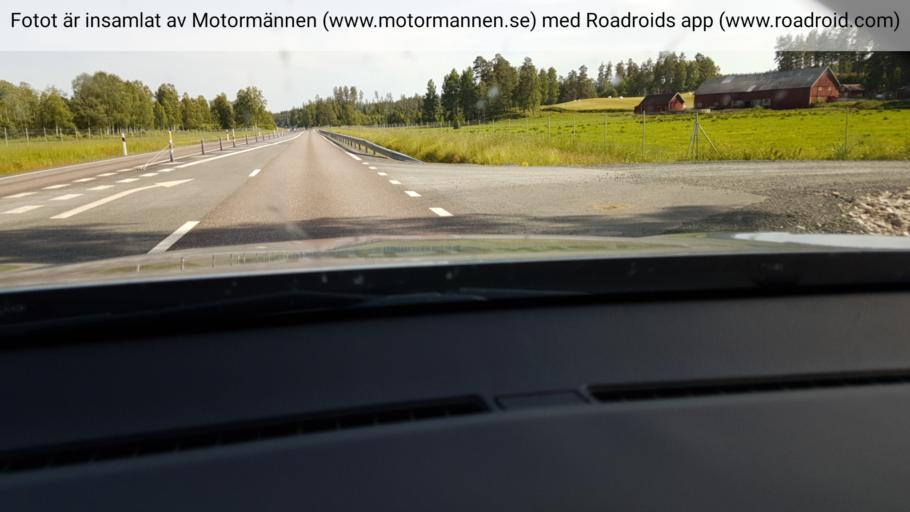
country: SE
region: Joenkoeping
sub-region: Aneby Kommun
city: Aneby
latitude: 57.8050
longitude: 14.8665
